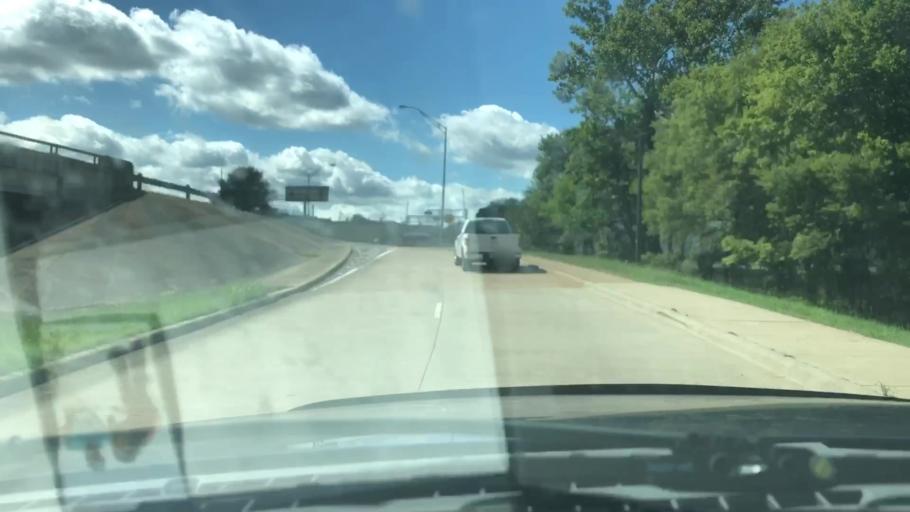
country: US
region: Texas
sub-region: Bowie County
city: Texarkana
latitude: 33.4202
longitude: -94.0512
